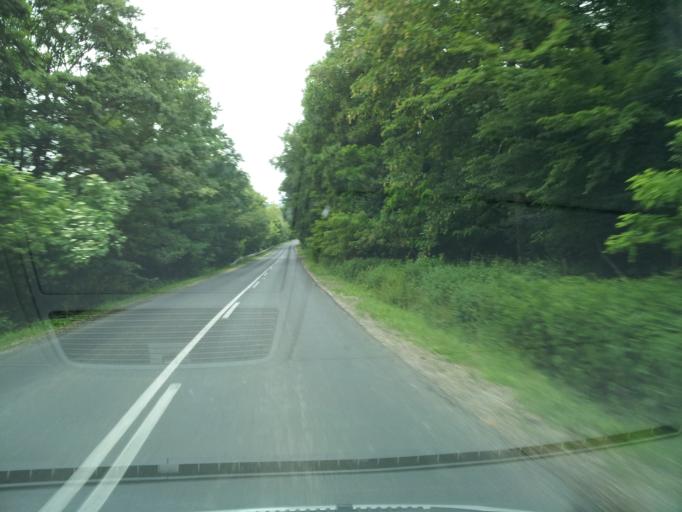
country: HU
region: Pest
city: Pilisszentkereszt
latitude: 47.6803
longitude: 18.9366
